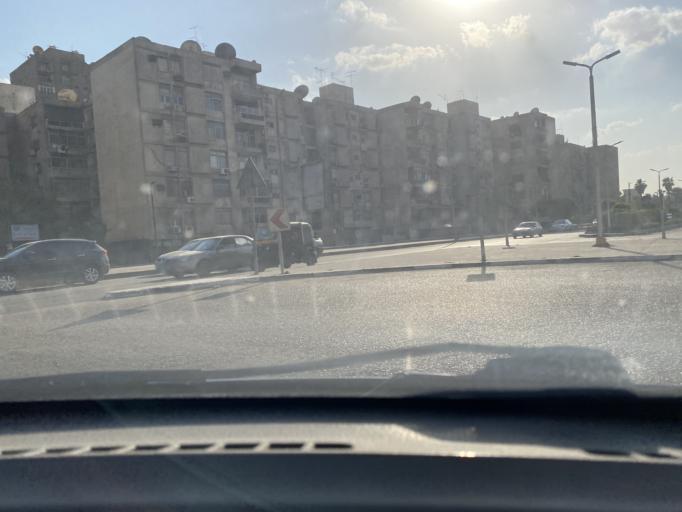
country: EG
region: Muhafazat al Qahirah
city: Cairo
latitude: 30.1035
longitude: 31.2994
